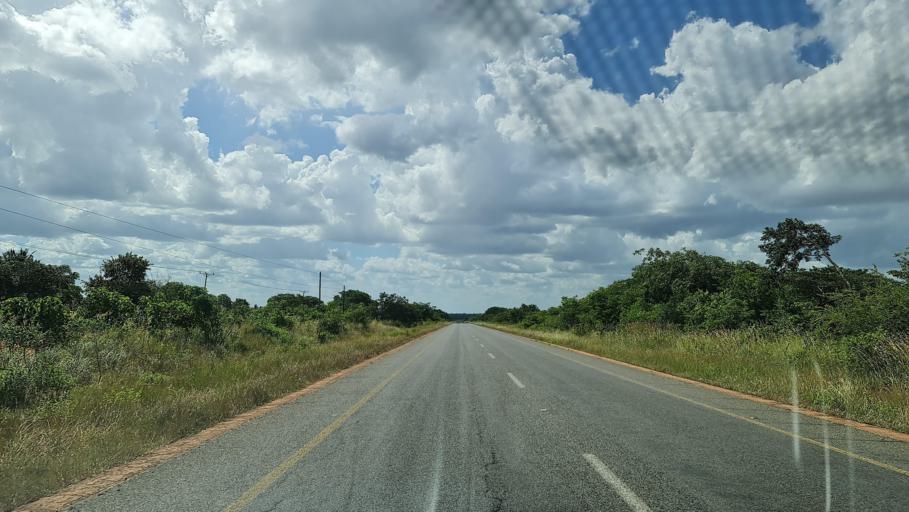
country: MZ
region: Inhambane
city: Maxixe
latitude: -22.9695
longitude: 35.2165
